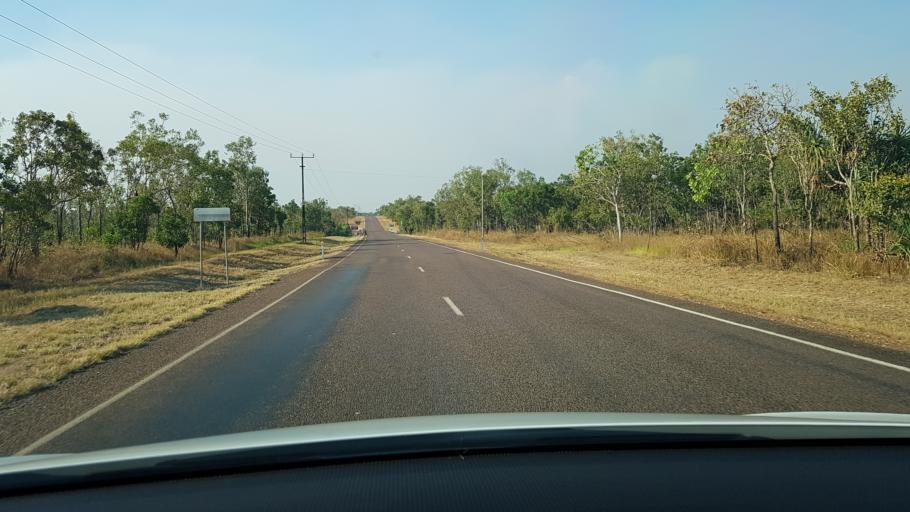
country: AU
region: Northern Territory
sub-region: Litchfield
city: McMinns Lagoon
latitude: -12.6955
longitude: 131.0217
